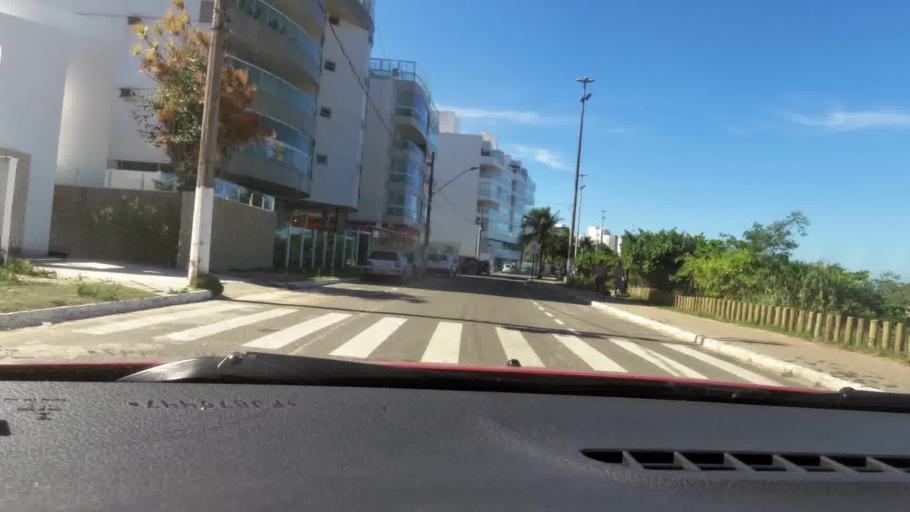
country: BR
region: Espirito Santo
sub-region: Guarapari
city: Guarapari
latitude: -20.7335
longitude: -40.5319
